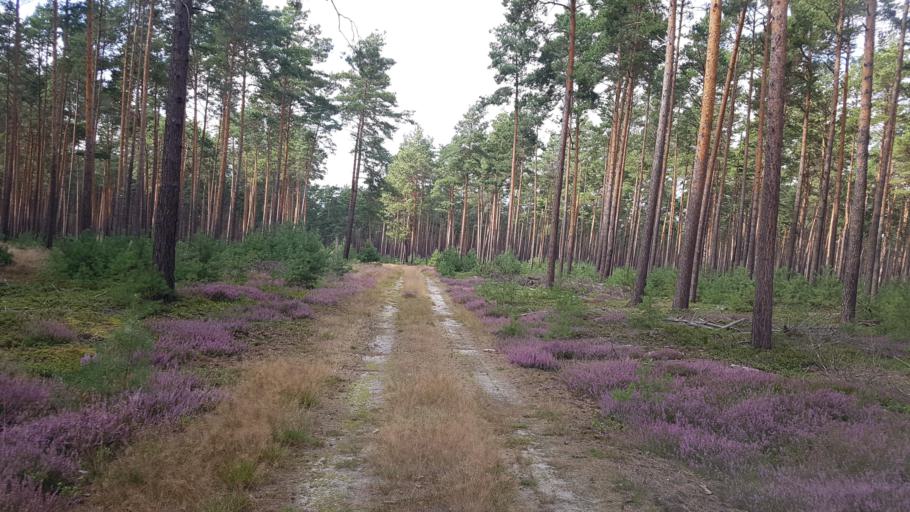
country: DE
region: Brandenburg
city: Schonborn
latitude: 51.6519
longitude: 13.4804
